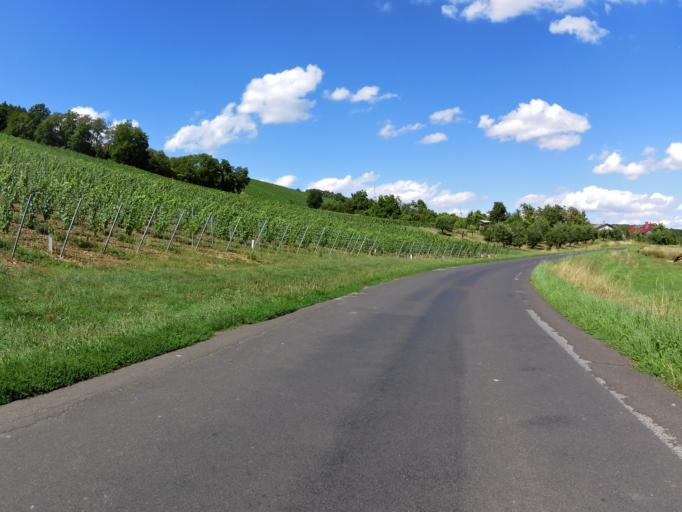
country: DE
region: Bavaria
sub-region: Regierungsbezirk Unterfranken
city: Prosselsheim
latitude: 49.8783
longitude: 10.1533
